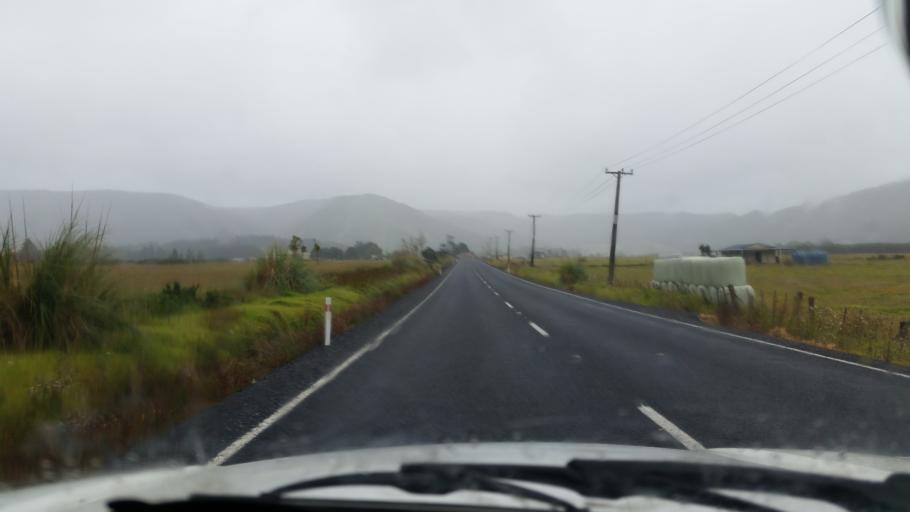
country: NZ
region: Northland
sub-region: Far North District
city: Ahipara
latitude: -35.1774
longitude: 173.1728
